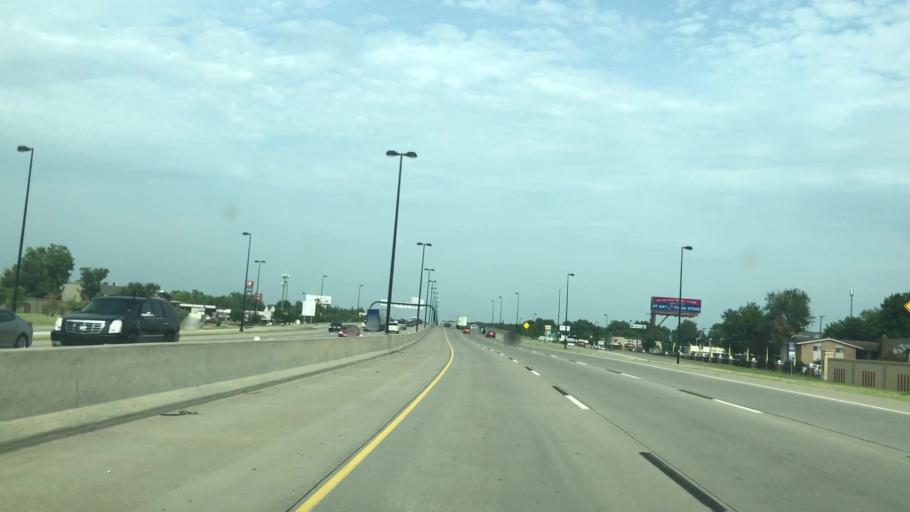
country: US
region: Oklahoma
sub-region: Tulsa County
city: Tulsa
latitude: 36.0894
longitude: -95.9802
